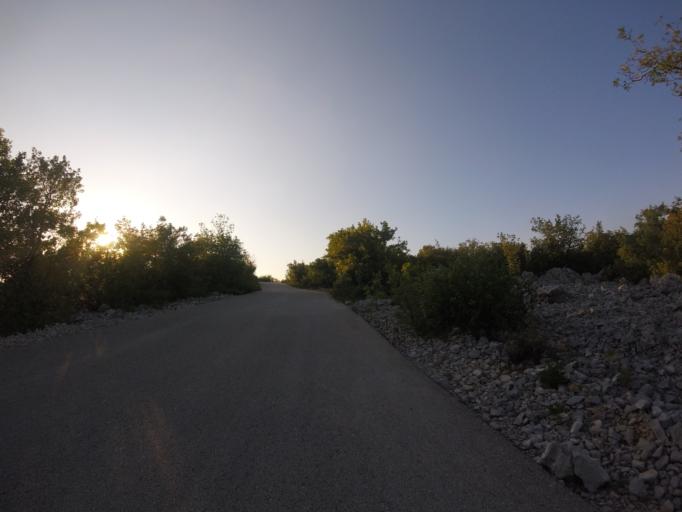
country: HR
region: Primorsko-Goranska
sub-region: Grad Crikvenica
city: Jadranovo
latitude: 45.2078
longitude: 14.6448
